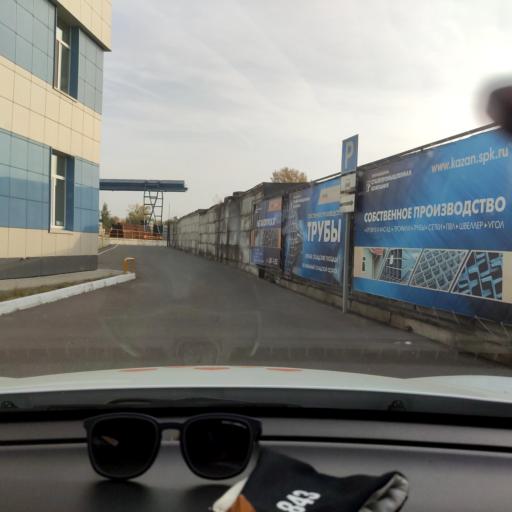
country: RU
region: Tatarstan
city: Staroye Arakchino
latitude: 55.8344
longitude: 49.0277
